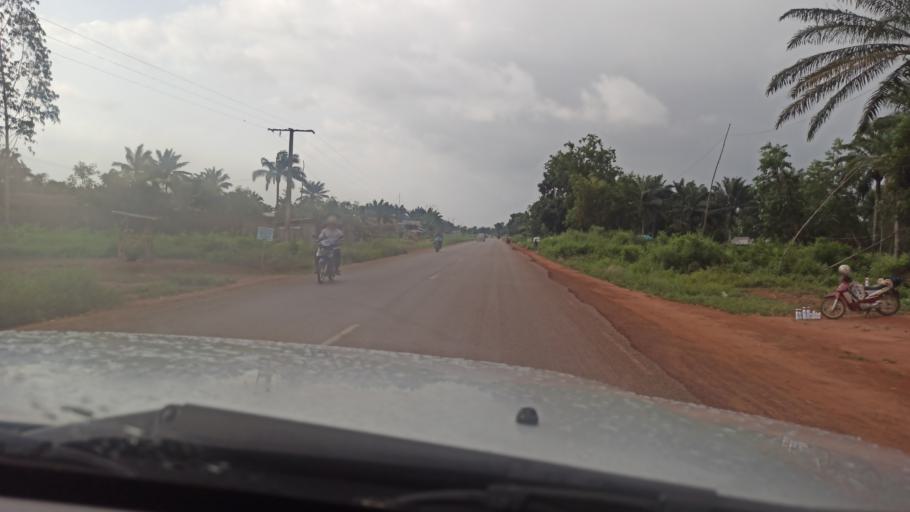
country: BJ
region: Queme
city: Porto-Novo
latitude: 6.5660
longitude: 2.5805
